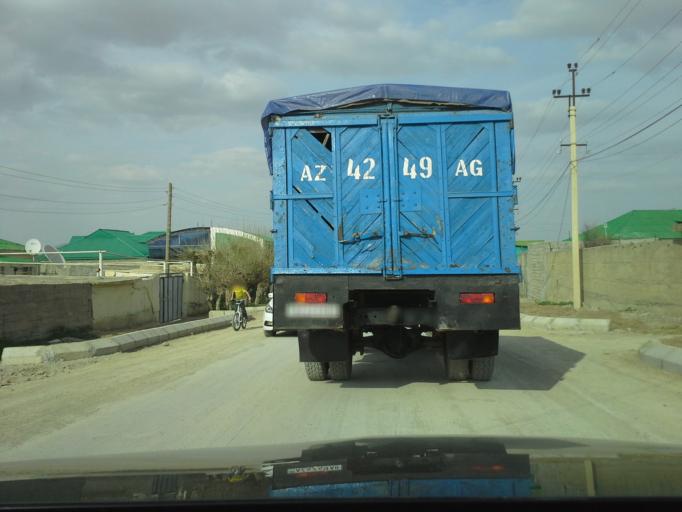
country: TM
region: Ahal
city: Abadan
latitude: 37.9575
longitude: 58.2077
